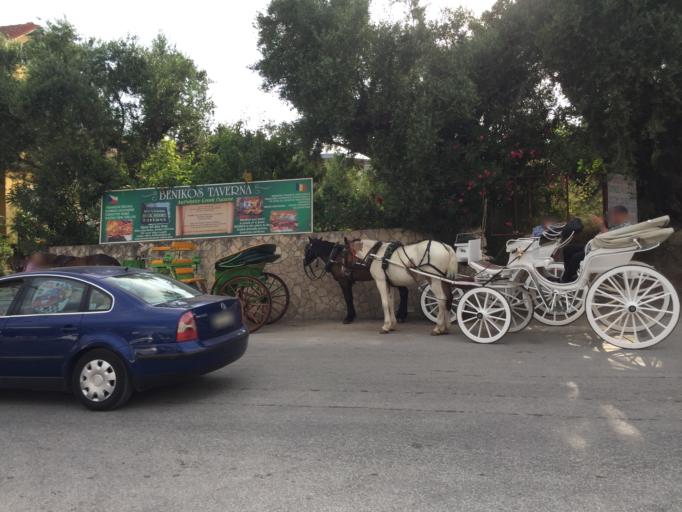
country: GR
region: Ionian Islands
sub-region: Nomos Zakynthou
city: Gaitanion
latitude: 37.8129
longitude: 20.8723
